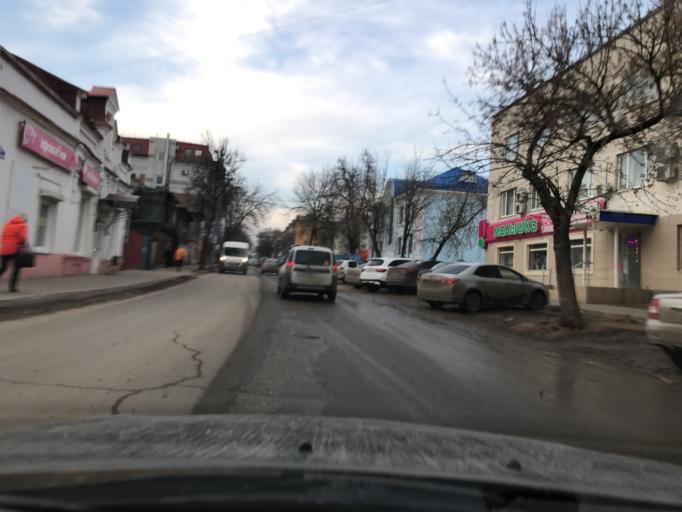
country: RU
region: Kaluga
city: Kaluga
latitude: 54.5122
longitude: 36.2462
